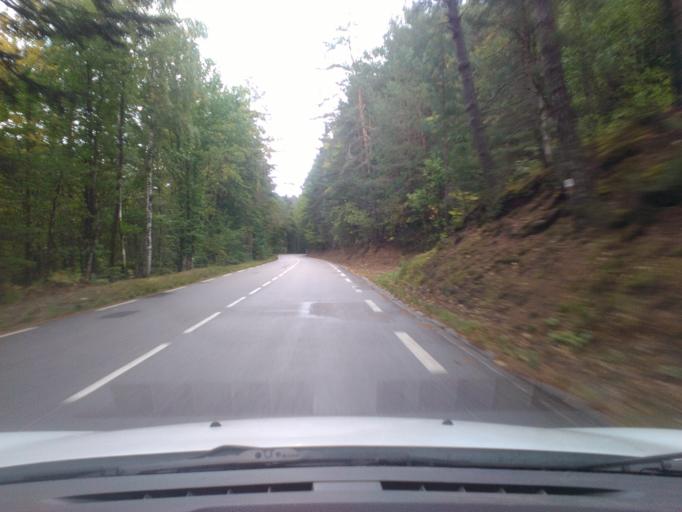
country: FR
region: Lorraine
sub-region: Departement des Vosges
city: Taintrux
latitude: 48.2707
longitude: 6.8788
